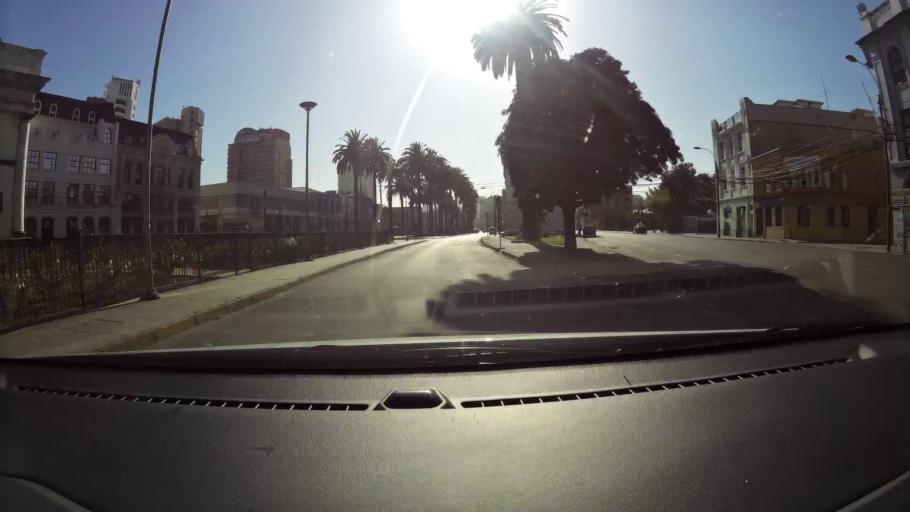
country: CL
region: Valparaiso
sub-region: Provincia de Valparaiso
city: Valparaiso
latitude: -33.0448
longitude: -71.6204
